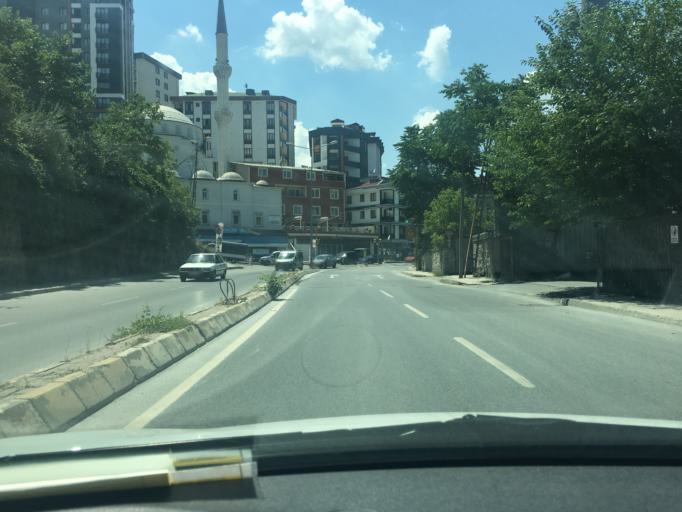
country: TR
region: Istanbul
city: Sisli
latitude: 41.0869
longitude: 28.9379
